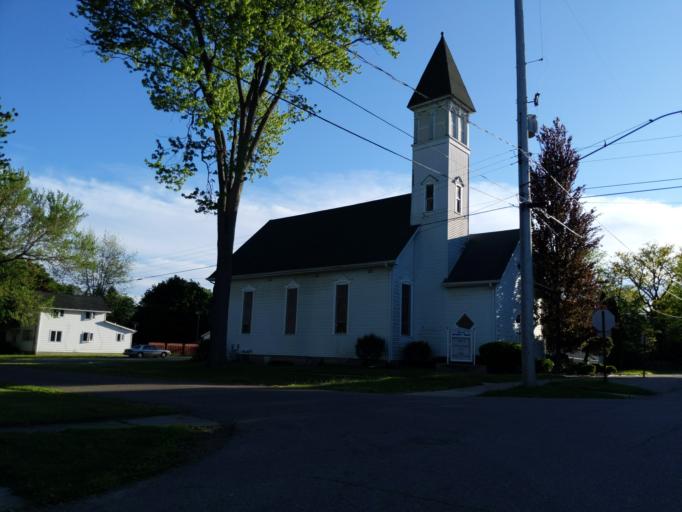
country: US
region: Michigan
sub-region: Ingham County
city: Stockbridge
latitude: 42.4502
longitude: -84.1776
